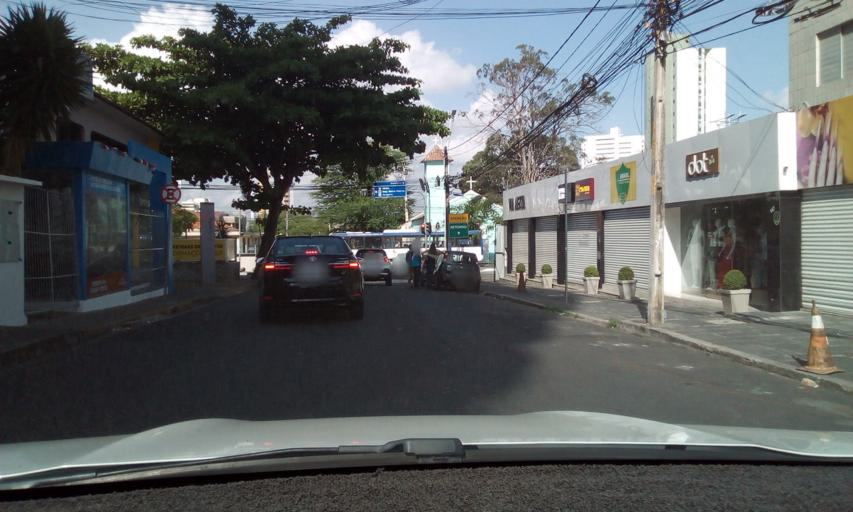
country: BR
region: Pernambuco
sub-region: Caruaru
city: Caruaru
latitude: -8.2800
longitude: -35.9722
